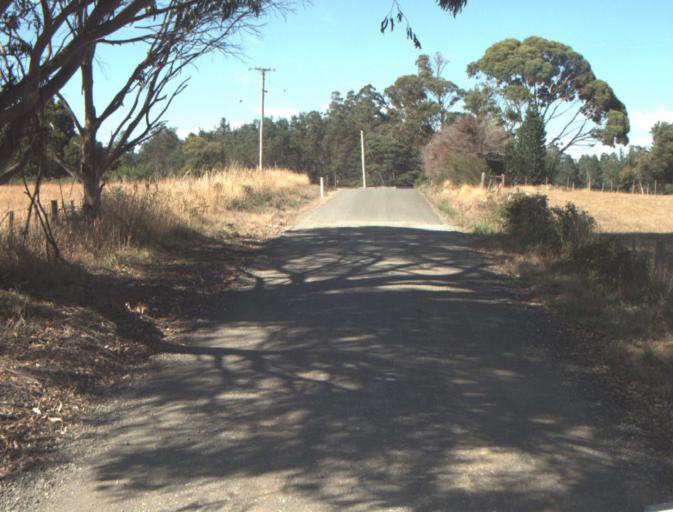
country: AU
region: Tasmania
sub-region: Launceston
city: Mayfield
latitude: -41.1771
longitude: 147.2156
